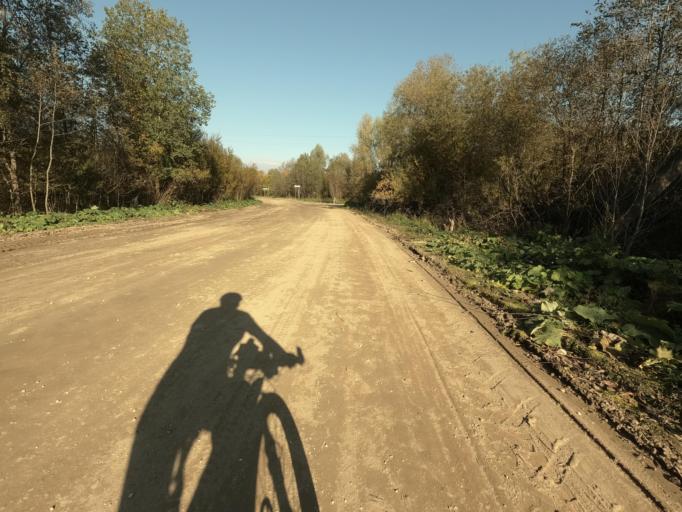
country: RU
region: Novgorod
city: Batetskiy
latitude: 58.8797
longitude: 30.7274
